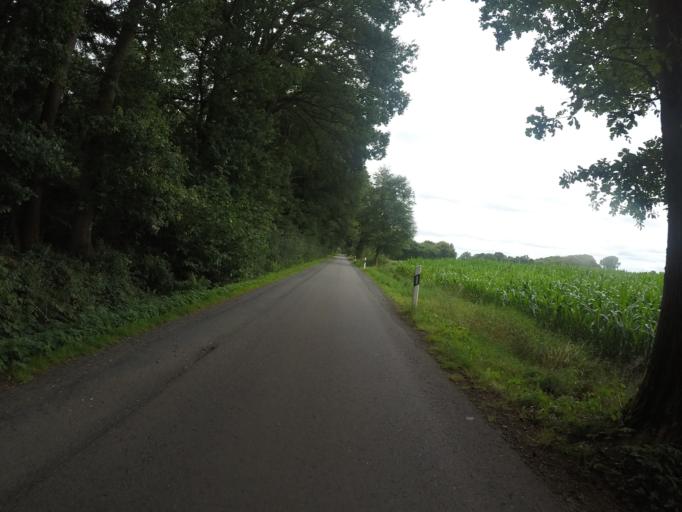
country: DE
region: Lower Saxony
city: Himmelpforten
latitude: 53.6103
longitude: 9.3227
